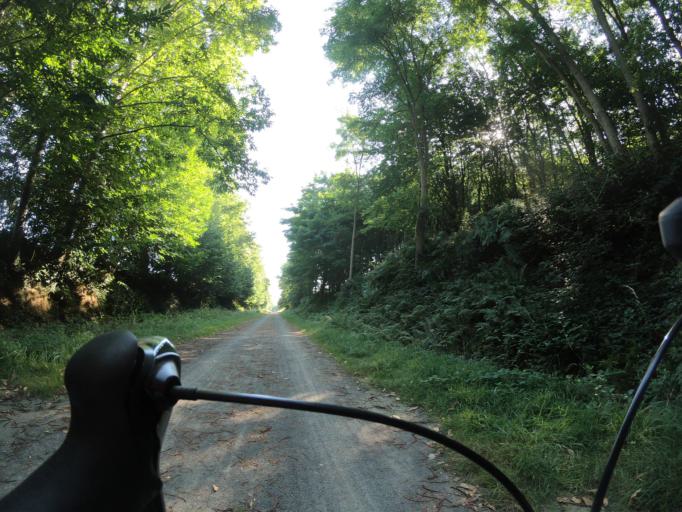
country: FR
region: Lower Normandy
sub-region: Departement de la Manche
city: Parigny
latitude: 48.5990
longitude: -1.0544
